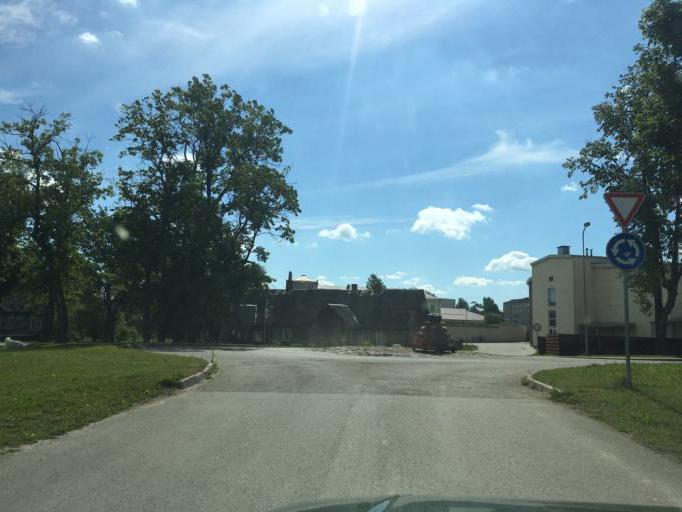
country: LV
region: Balvu Rajons
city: Balvi
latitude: 57.1337
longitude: 27.2656
